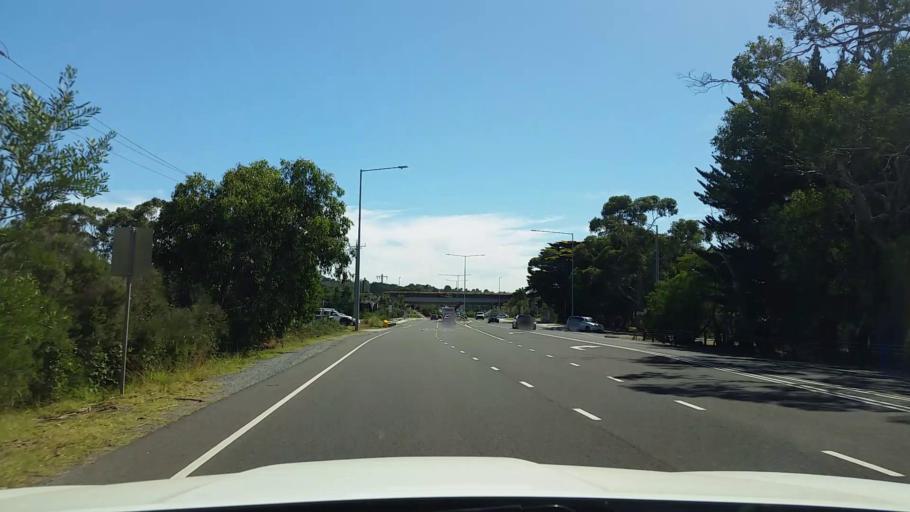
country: AU
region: Victoria
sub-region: Mornington Peninsula
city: Baxter
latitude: -38.1992
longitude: 145.1513
